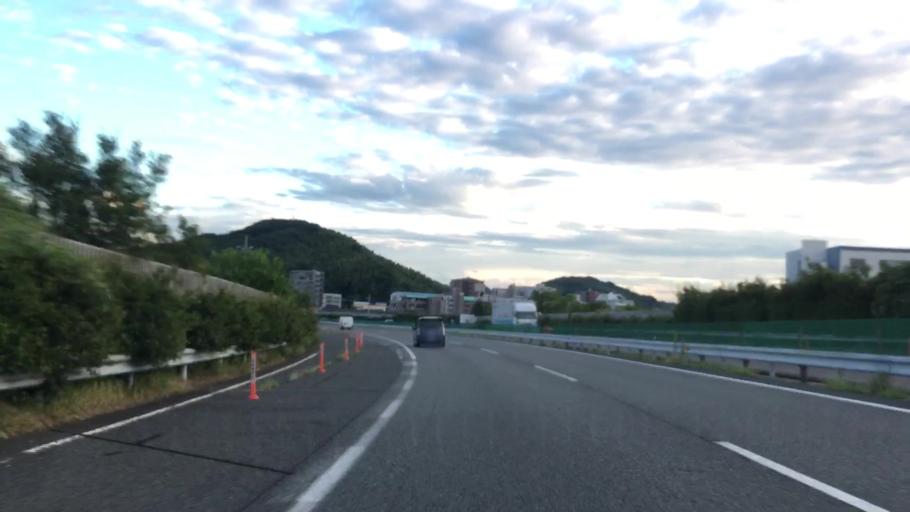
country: JP
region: Yamaguchi
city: Shimonoseki
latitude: 34.0139
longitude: 130.9557
